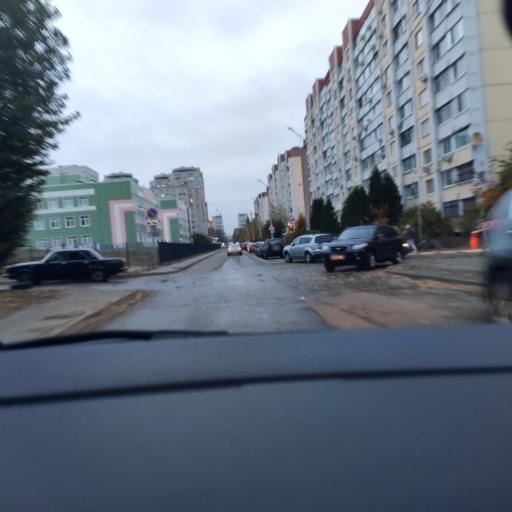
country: RU
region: Voronezj
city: Voronezh
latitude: 51.7086
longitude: 39.1871
